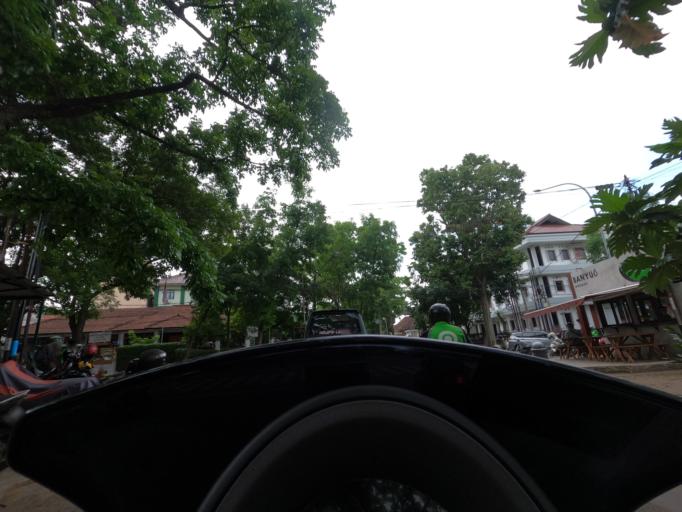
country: ID
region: West Java
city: Bandung
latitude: -6.9117
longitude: 107.6175
